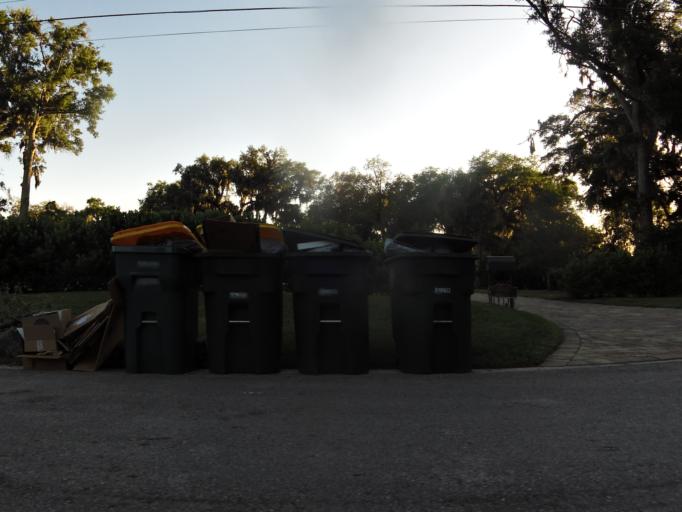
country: US
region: Florida
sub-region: Duval County
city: Jacksonville
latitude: 30.2711
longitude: -81.6520
